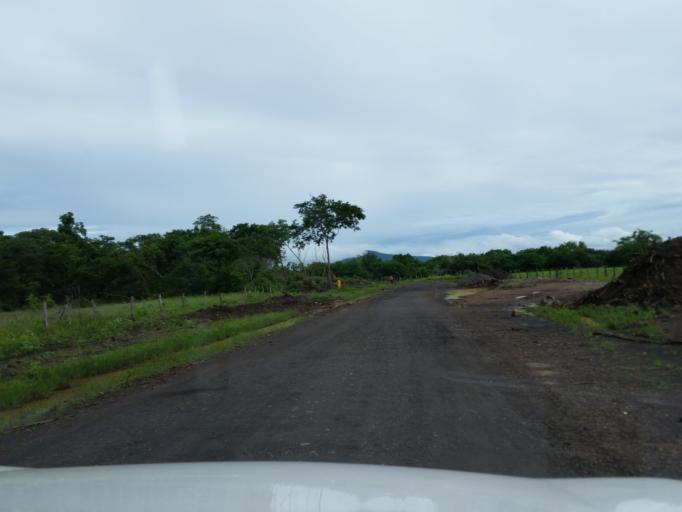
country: NI
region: Leon
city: Larreynaga
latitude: 12.5630
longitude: -86.6225
